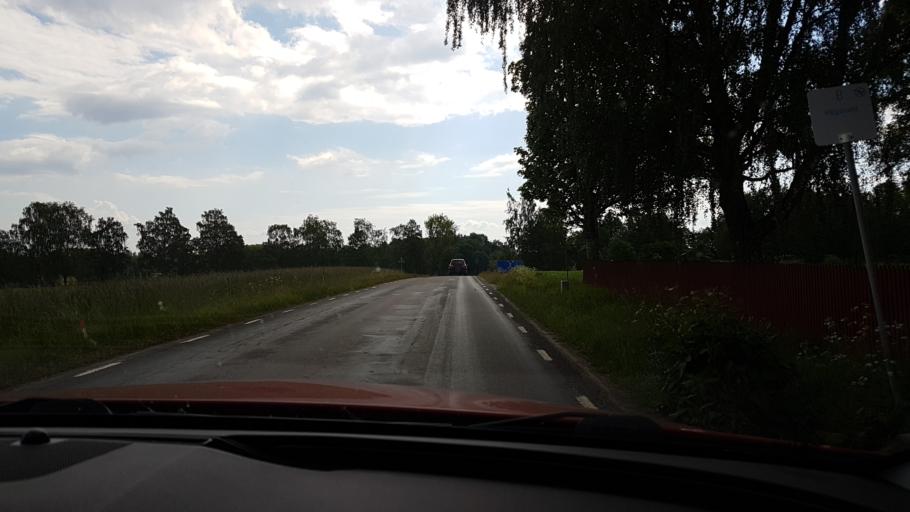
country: SE
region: Vaestra Goetaland
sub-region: Hjo Kommun
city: Hjo
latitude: 58.3059
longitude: 14.2458
